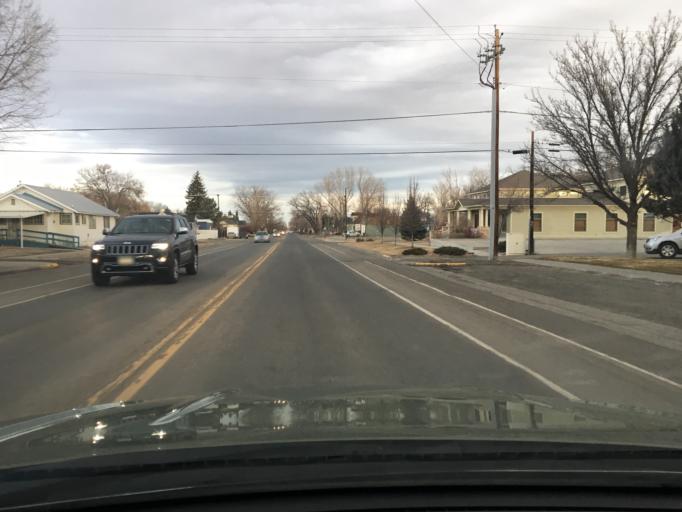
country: US
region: Colorado
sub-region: Montrose County
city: Montrose
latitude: 38.4773
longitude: -107.8705
